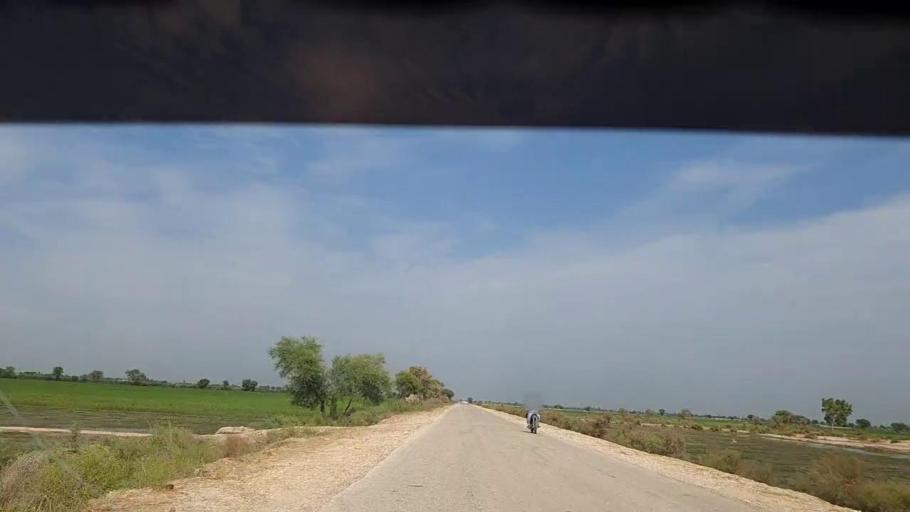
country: PK
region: Sindh
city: Thul
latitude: 28.1930
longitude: 68.7712
